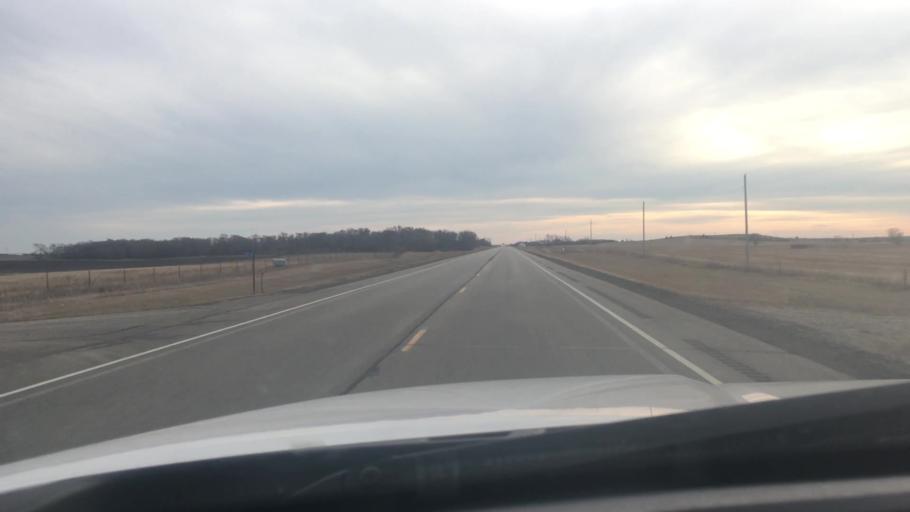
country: US
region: Minnesota
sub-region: Otter Tail County
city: Perham
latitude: 46.3355
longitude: -95.7185
